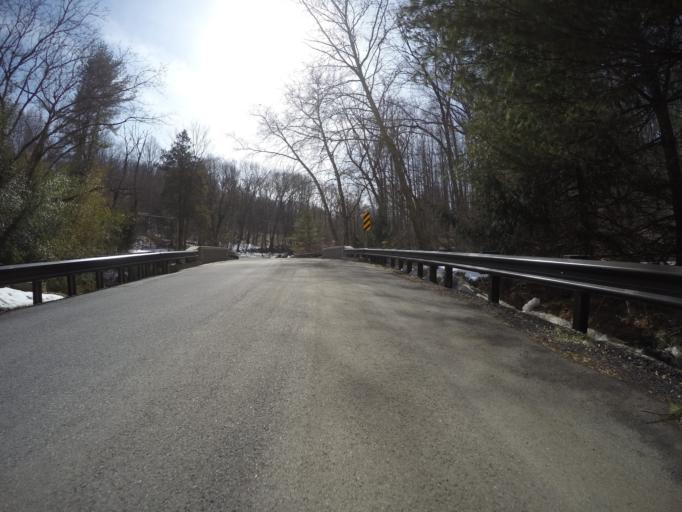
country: US
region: Maryland
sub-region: Baltimore County
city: Hunt Valley
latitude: 39.5161
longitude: -76.6578
